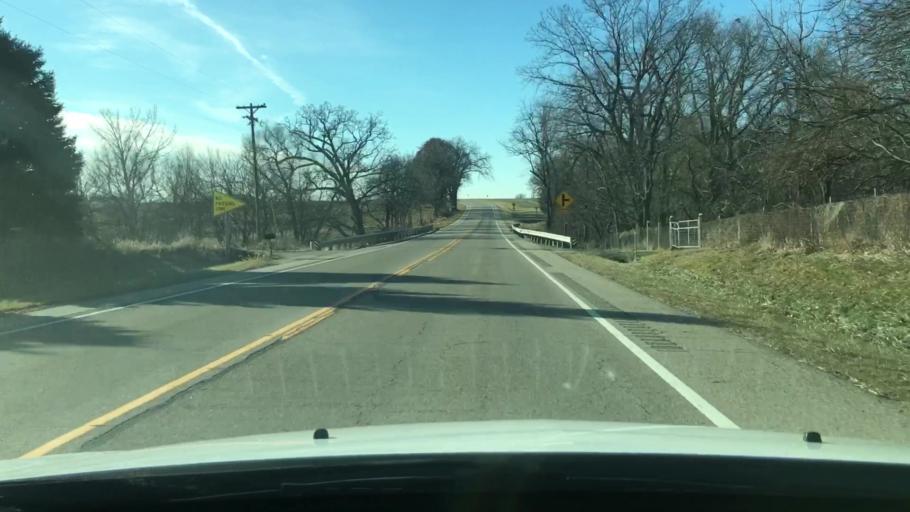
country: US
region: Illinois
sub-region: Woodford County
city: Washburn
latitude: 40.8650
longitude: -89.3288
